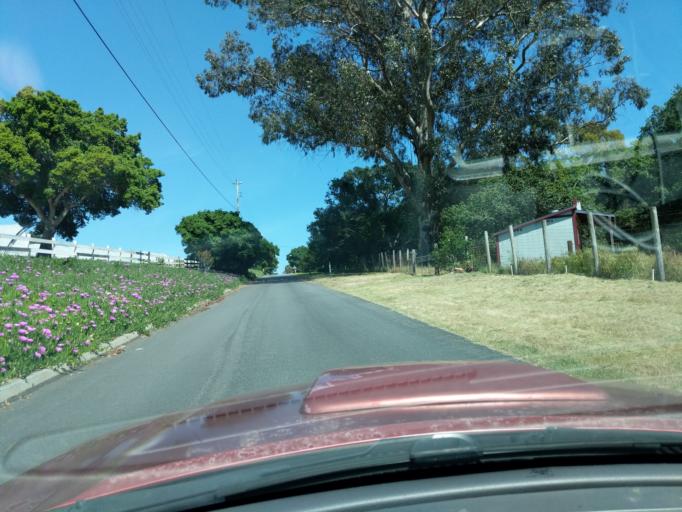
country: US
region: California
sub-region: Monterey County
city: Las Lomas
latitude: 36.8703
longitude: -121.6880
